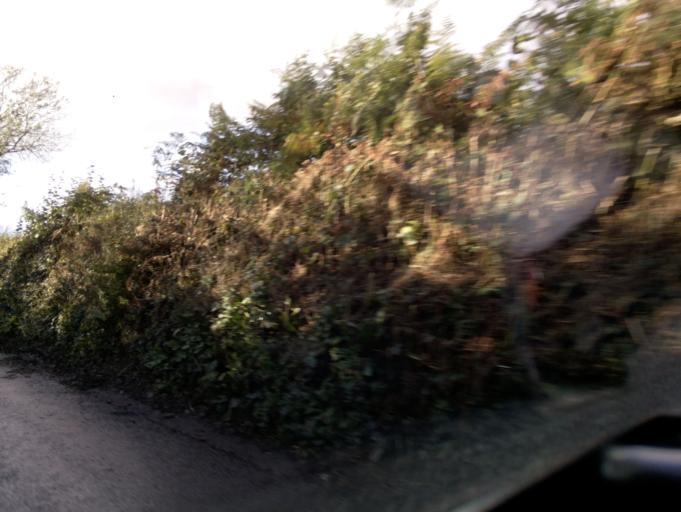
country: GB
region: England
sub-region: Devon
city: Totnes
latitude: 50.3586
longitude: -3.7305
